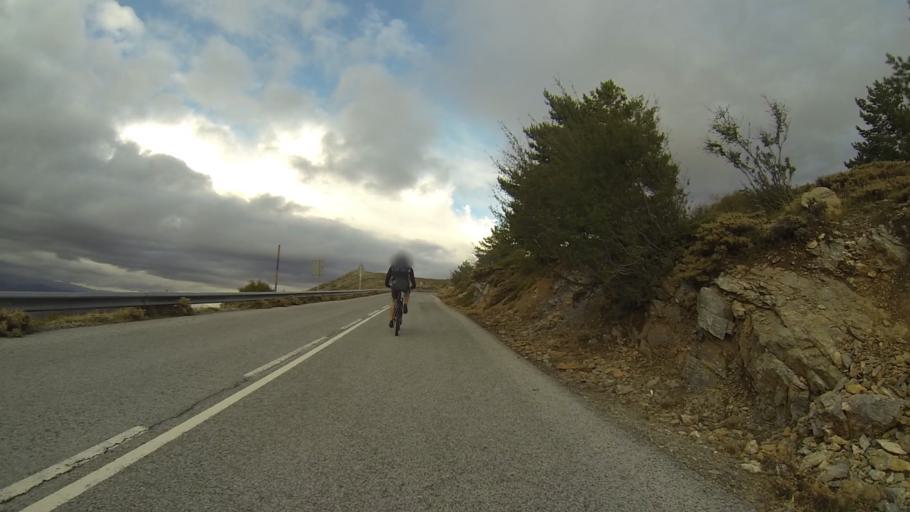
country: ES
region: Andalusia
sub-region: Provincia de Granada
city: Guejar-Sierra
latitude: 37.1193
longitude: -3.4389
